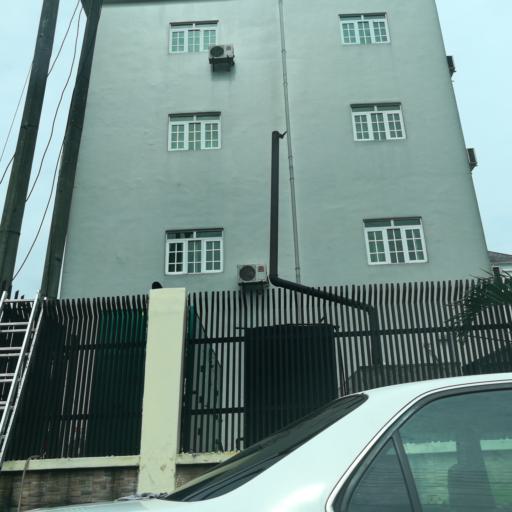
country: NG
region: Rivers
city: Port Harcourt
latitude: 4.8243
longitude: 6.9863
